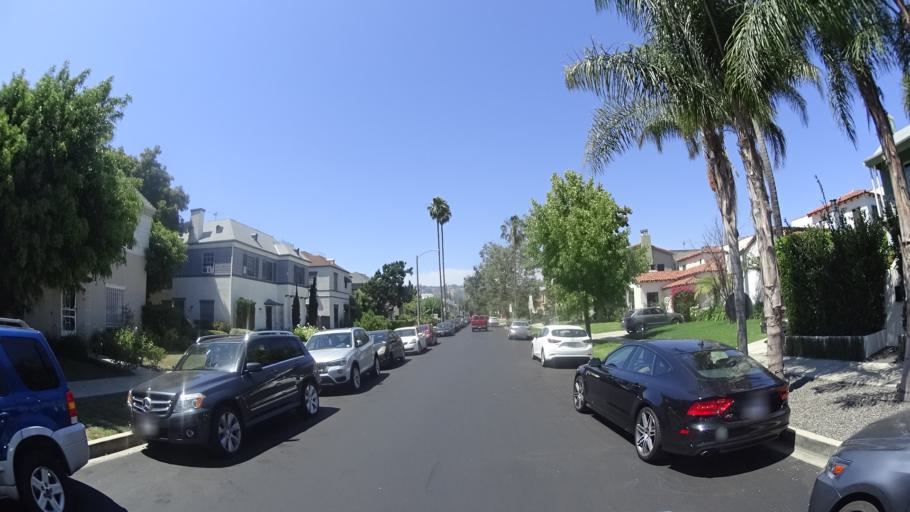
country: US
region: California
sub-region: Los Angeles County
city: West Hollywood
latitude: 34.0745
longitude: -118.3690
